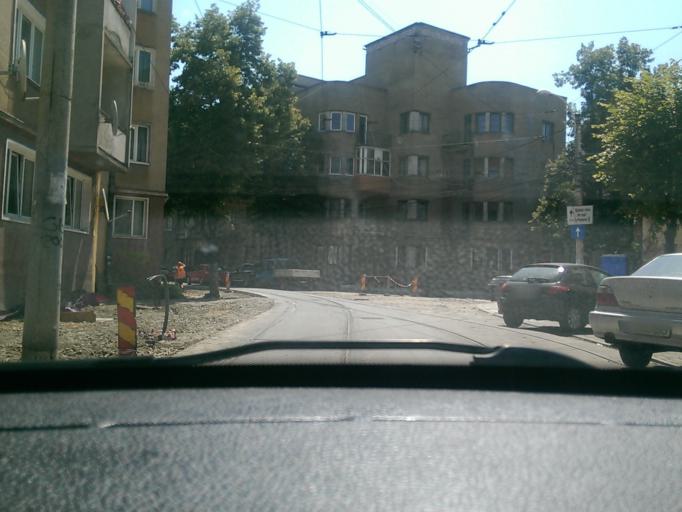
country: RO
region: Cluj
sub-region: Municipiul Cluj-Napoca
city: Cluj-Napoca
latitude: 46.7833
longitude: 23.5861
